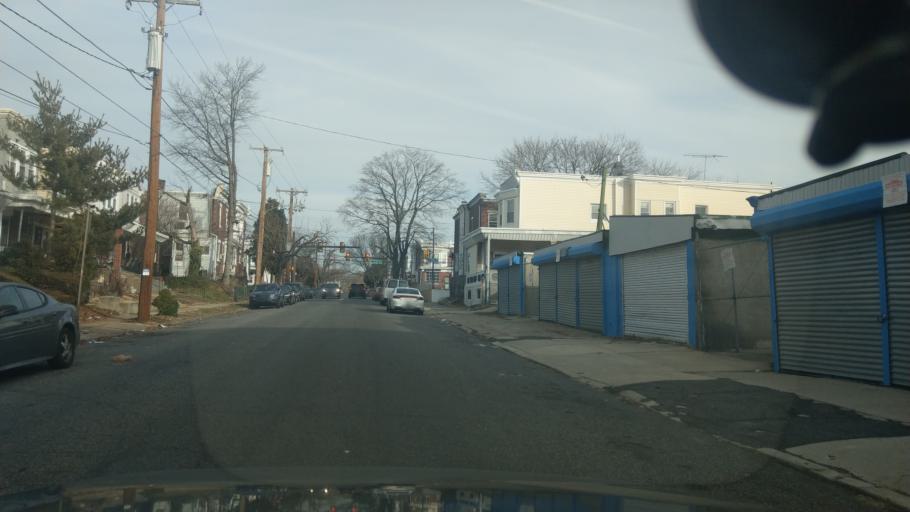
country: US
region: Pennsylvania
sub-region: Montgomery County
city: Jenkintown
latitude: 40.0359
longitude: -75.1326
